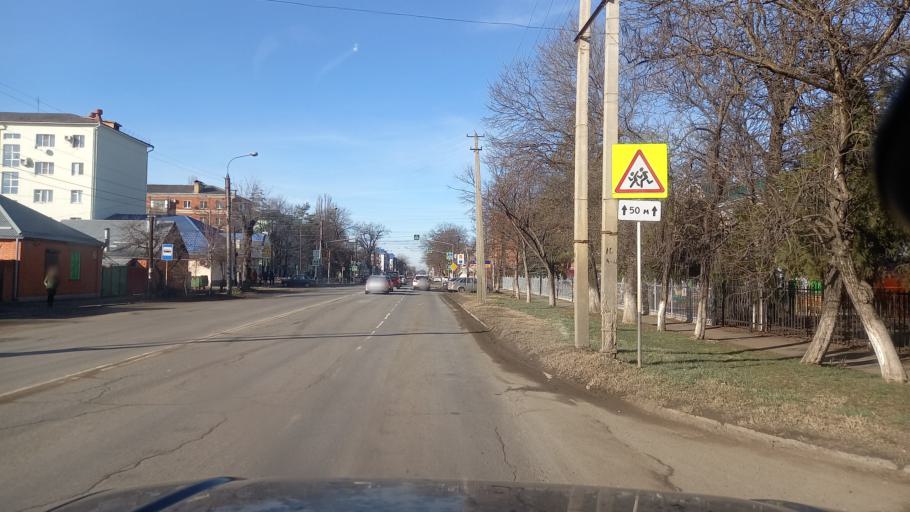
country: RU
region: Adygeya
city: Maykop
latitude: 44.6171
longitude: 40.1106
